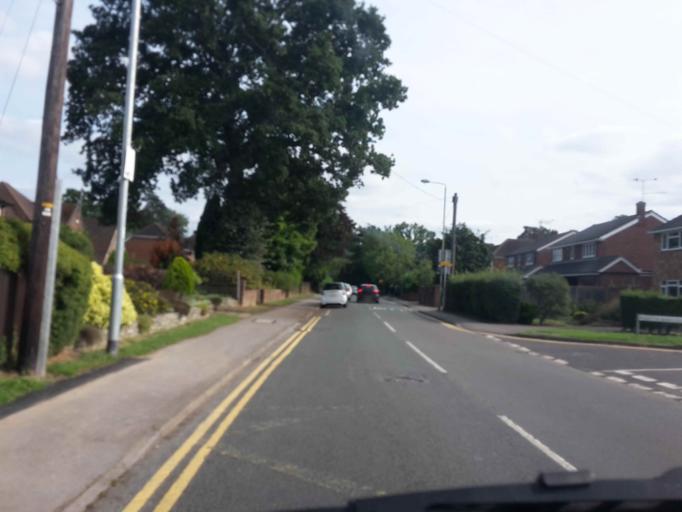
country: GB
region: England
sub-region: Wokingham
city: Wokingham
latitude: 51.4085
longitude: -0.8262
